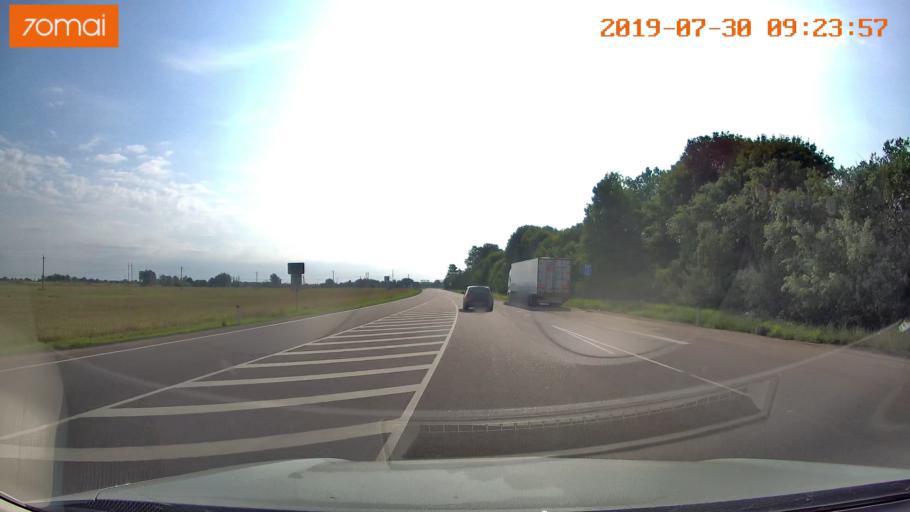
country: LT
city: Kybartai
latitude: 54.6328
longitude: 22.6842
